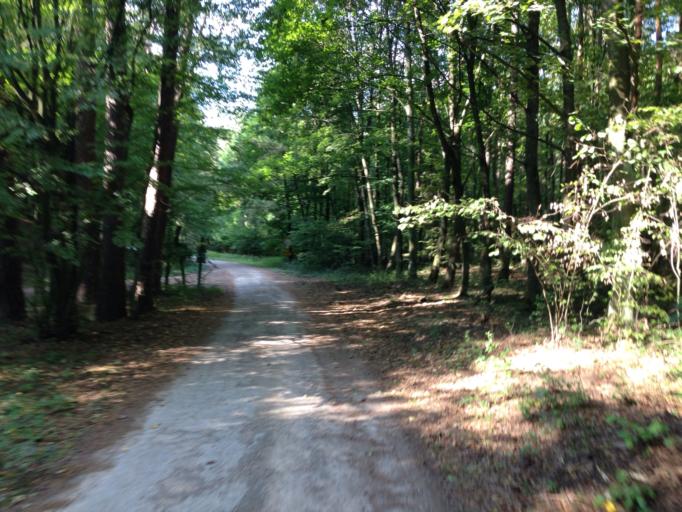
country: PL
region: Kujawsko-Pomorskie
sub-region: Powiat brodnicki
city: Gorzno
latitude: 53.1891
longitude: 19.6634
